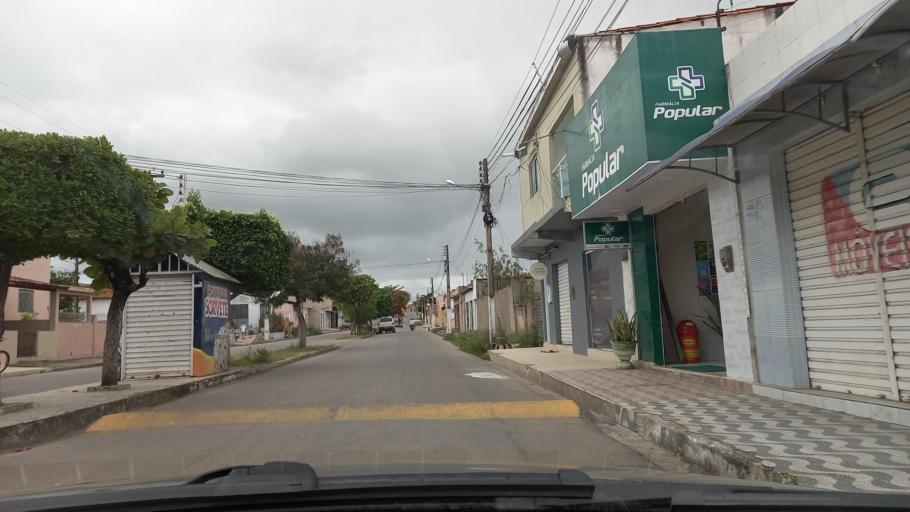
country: BR
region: Sergipe
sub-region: Caninde De Sao Francisco
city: Caninde de Sao Francisco
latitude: -9.6067
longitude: -37.7598
